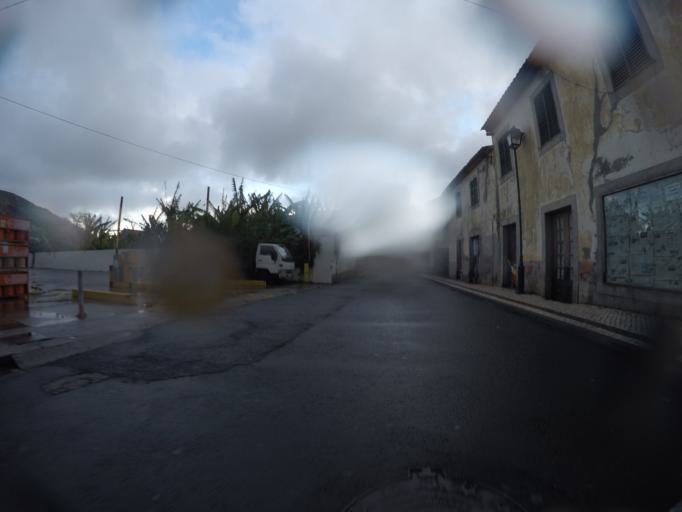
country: PT
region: Madeira
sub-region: Machico
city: Machico
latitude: 32.7195
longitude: -16.7675
